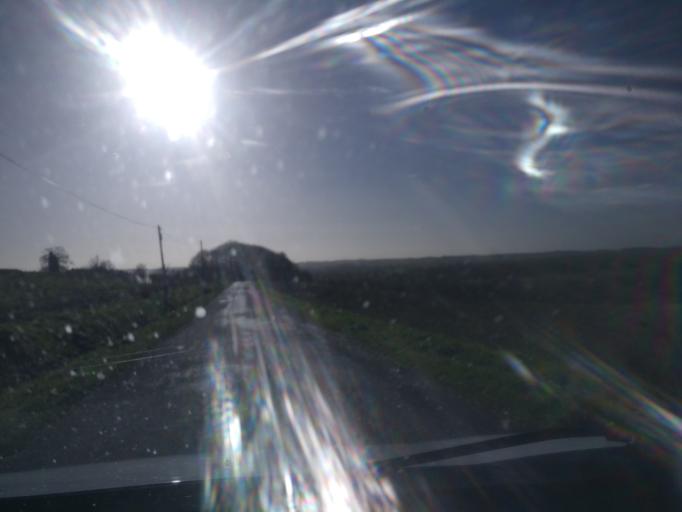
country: FR
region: Brittany
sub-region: Departement d'Ille-et-Vilaine
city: La Boussac
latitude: 48.5448
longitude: -1.6214
